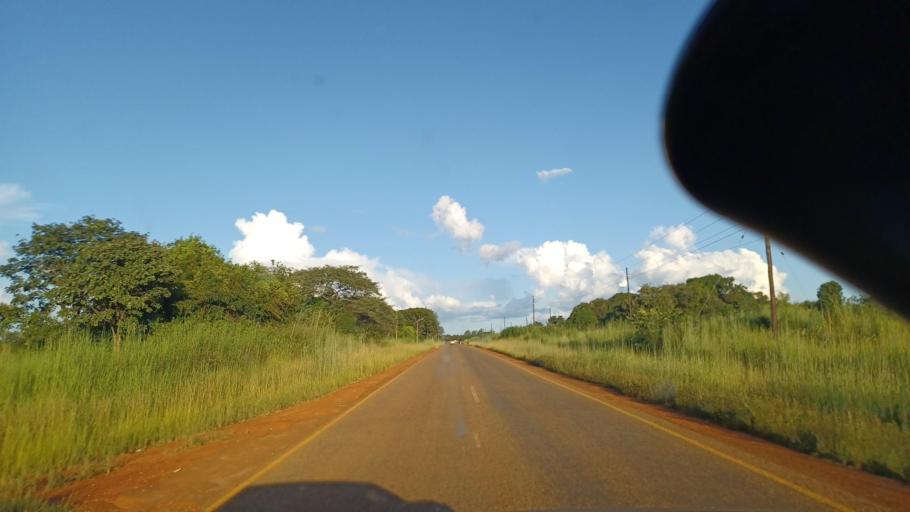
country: ZM
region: North-Western
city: Kalengwa
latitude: -13.1393
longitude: 25.0168
